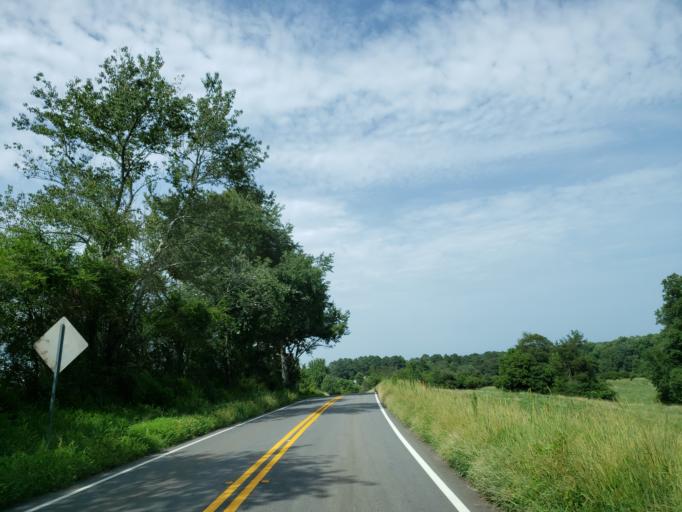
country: US
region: Georgia
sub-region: Cherokee County
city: Canton
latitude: 34.3046
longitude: -84.4524
